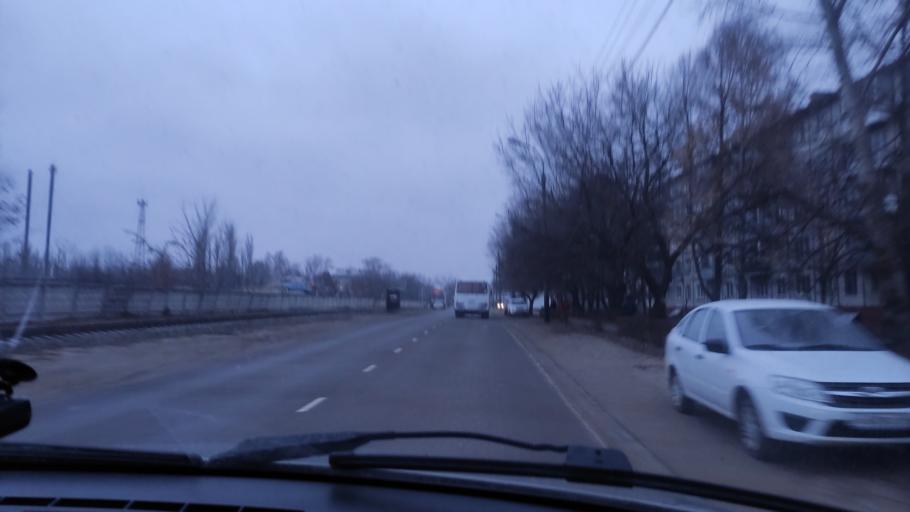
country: RU
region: Tambov
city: Pokrovo-Prigorodnoye
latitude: 52.7182
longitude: 41.3876
